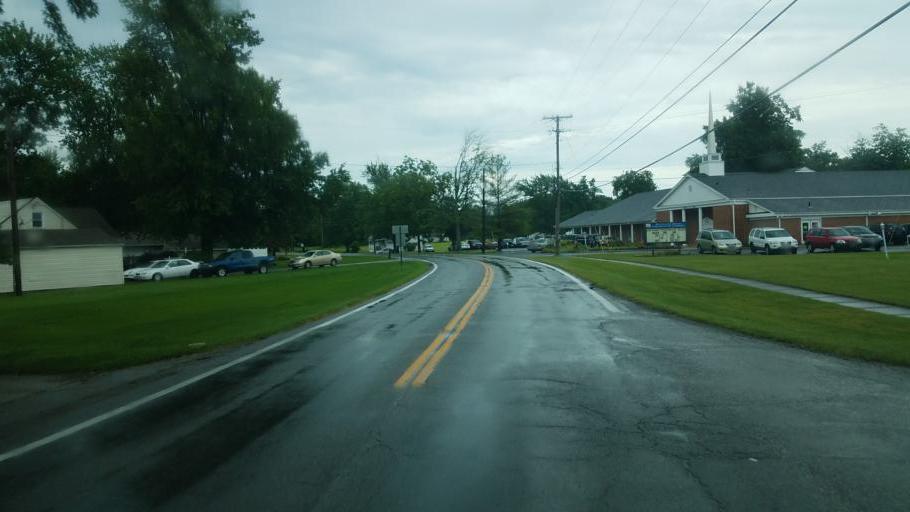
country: US
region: Ohio
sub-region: Marion County
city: Marion
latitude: 40.5756
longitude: -83.0982
